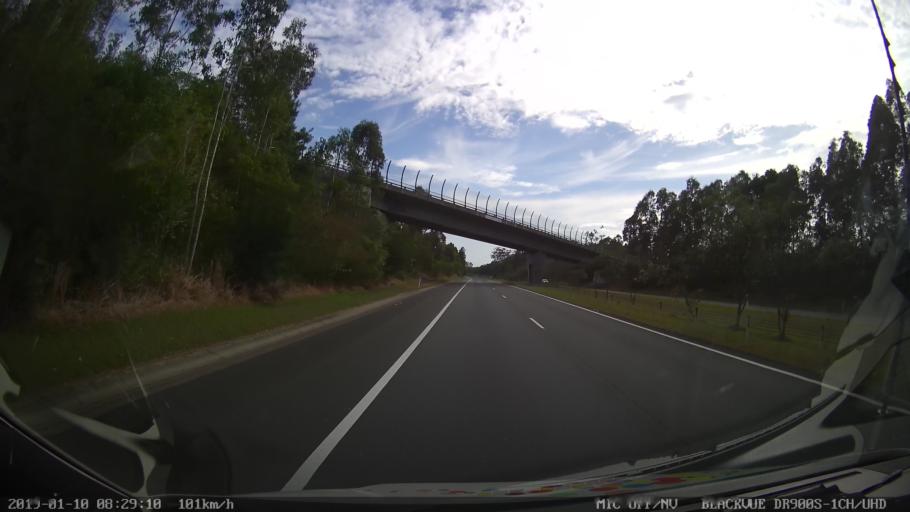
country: AU
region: New South Wales
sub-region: Coffs Harbour
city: Bonville
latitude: -30.3859
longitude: 153.0421
